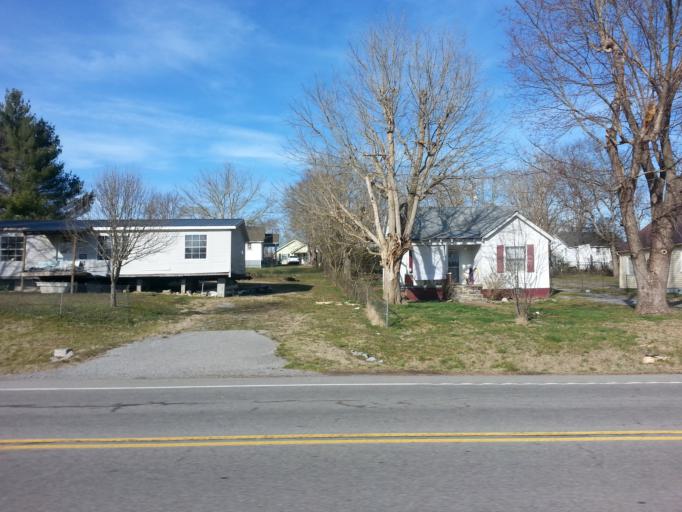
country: US
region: Tennessee
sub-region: Cannon County
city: Woodbury
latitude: 35.8217
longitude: -86.0501
